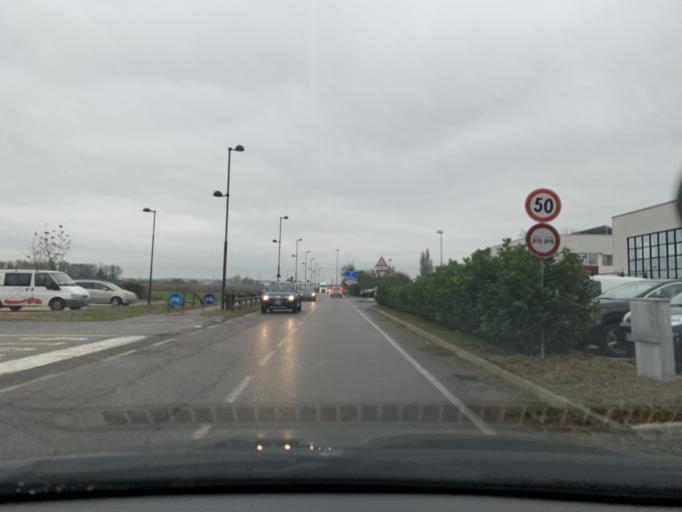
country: IT
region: Lombardy
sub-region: Provincia di Varese
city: Saronno
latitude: 45.6293
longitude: 9.0570
